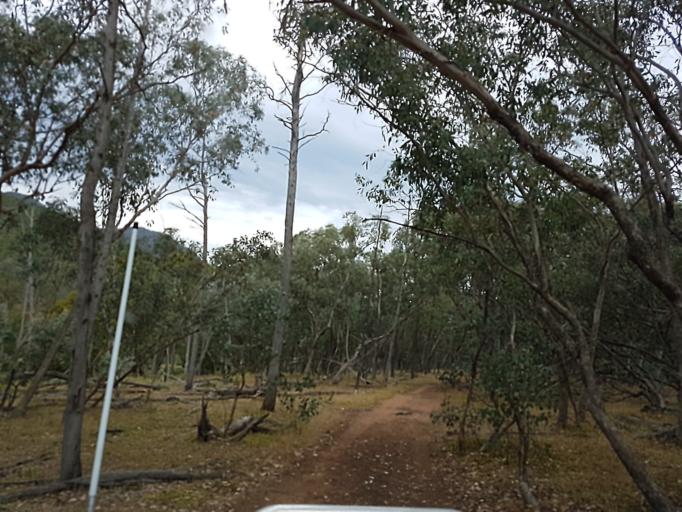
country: AU
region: New South Wales
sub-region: Snowy River
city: Jindabyne
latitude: -36.9561
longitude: 148.4084
